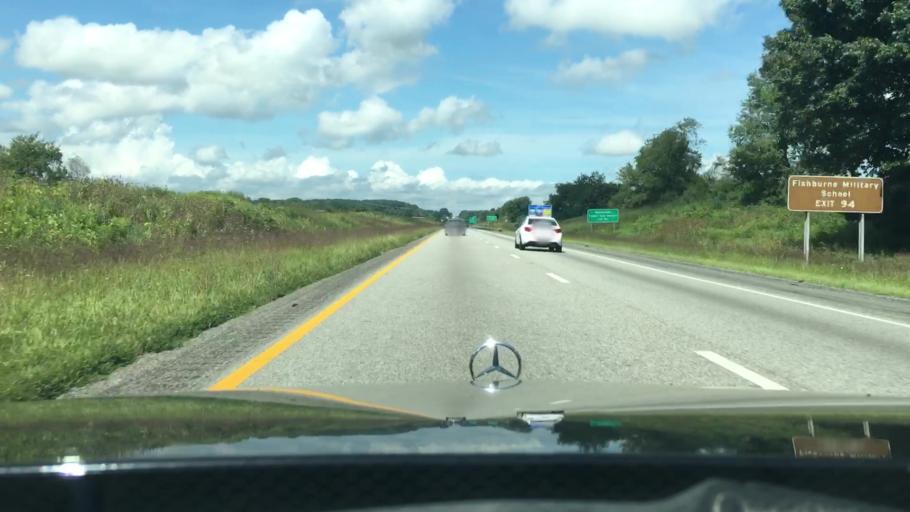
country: US
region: Virginia
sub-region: Augusta County
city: Lyndhurst
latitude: 38.0575
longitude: -78.9276
